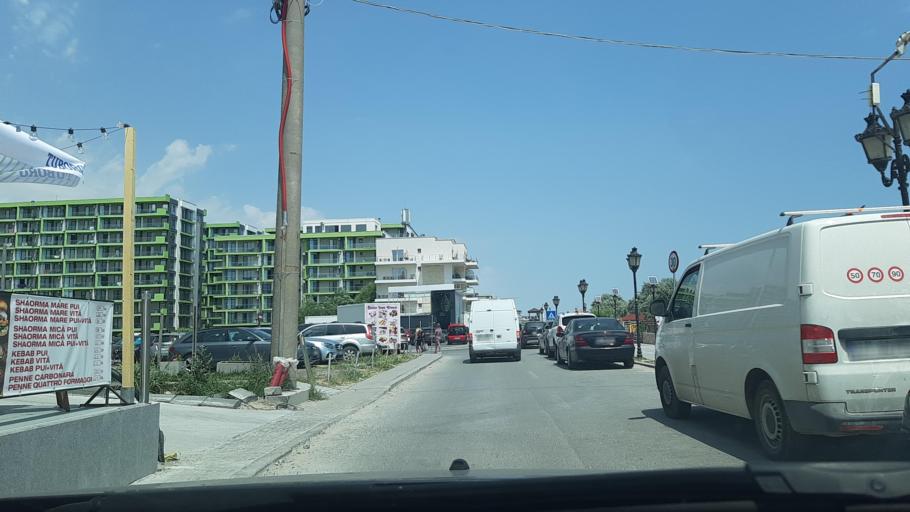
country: RO
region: Constanta
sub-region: Comuna Navodari
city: Navodari
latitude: 44.2991
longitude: 28.6258
